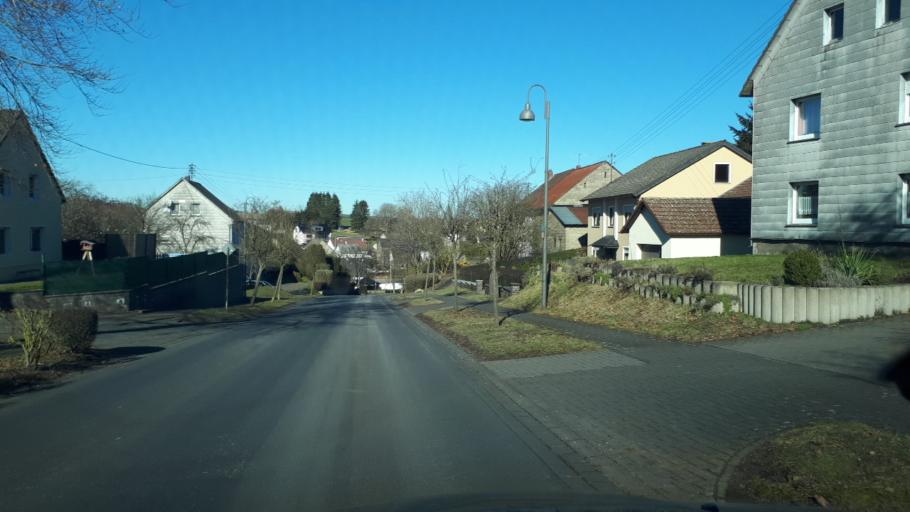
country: DE
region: Rheinland-Pfalz
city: Strotzbusch
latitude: 50.1083
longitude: 6.9660
